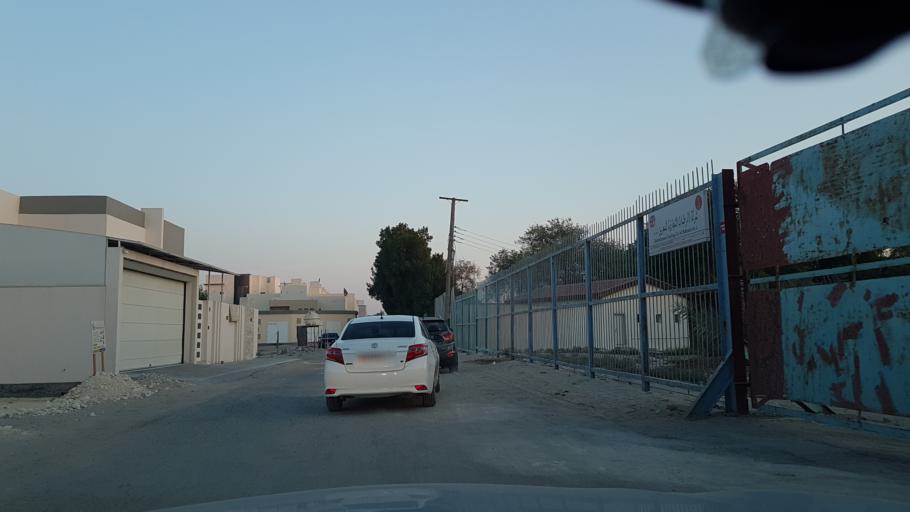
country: BH
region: Manama
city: Jidd Hafs
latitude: 26.2350
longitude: 50.5056
